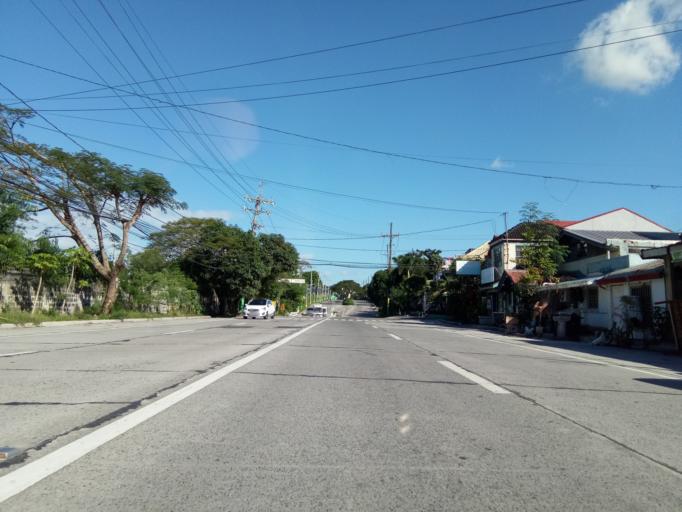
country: PH
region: Calabarzon
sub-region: Province of Cavite
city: Dasmarinas
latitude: 14.3514
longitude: 120.9559
